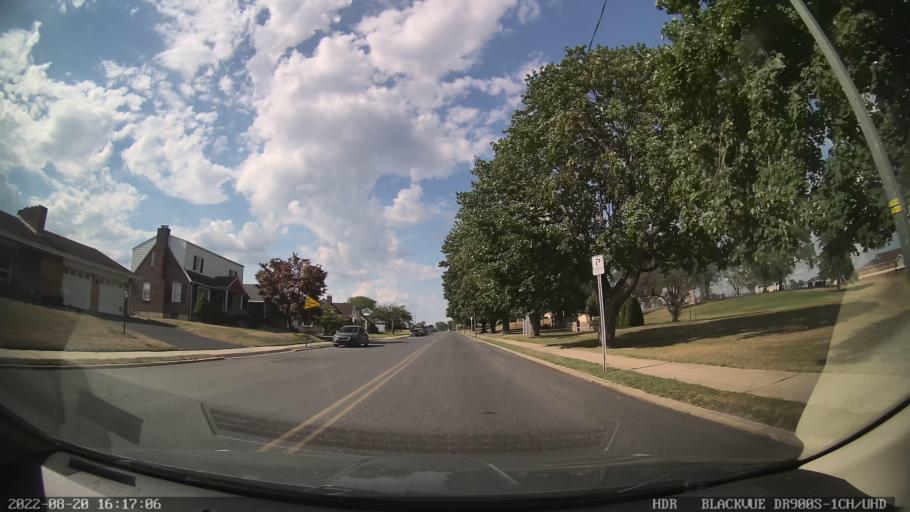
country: US
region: Pennsylvania
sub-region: Northampton County
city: Northampton
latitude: 40.6856
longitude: -75.4918
